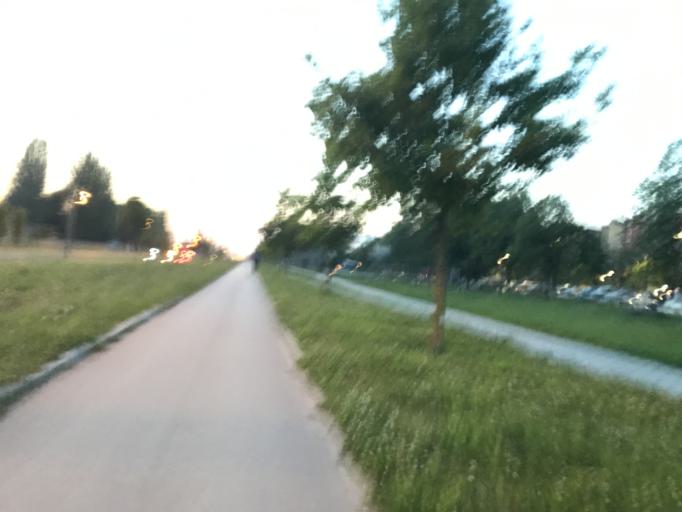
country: RS
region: Autonomna Pokrajina Vojvodina
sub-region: Juznobacki Okrug
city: Novi Sad
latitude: 45.2649
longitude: 19.8058
